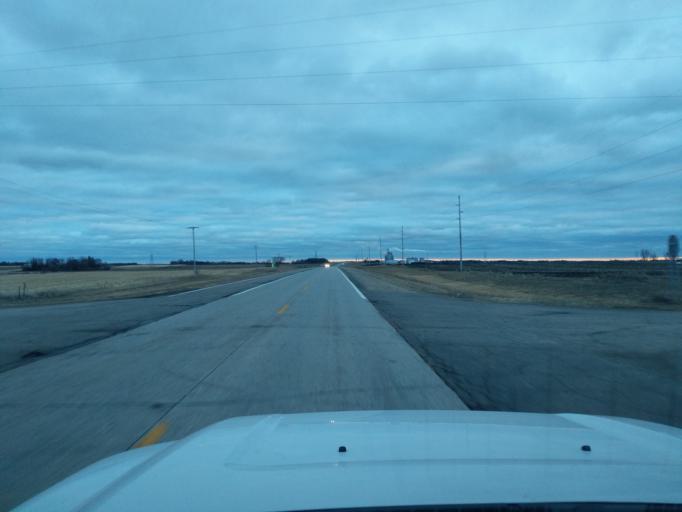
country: US
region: Minnesota
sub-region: Yellow Medicine County
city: Granite Falls
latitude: 44.8182
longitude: -95.4835
